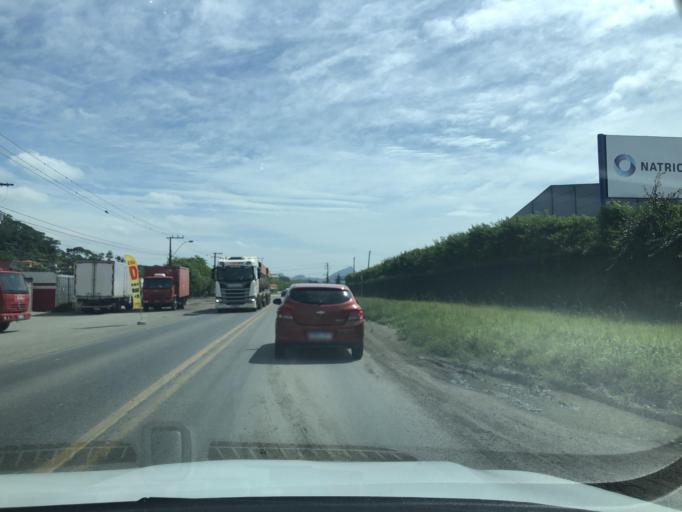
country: BR
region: Santa Catarina
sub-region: Sao Francisco Do Sul
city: Sao Francisco do Sul
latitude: -26.2566
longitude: -48.6220
